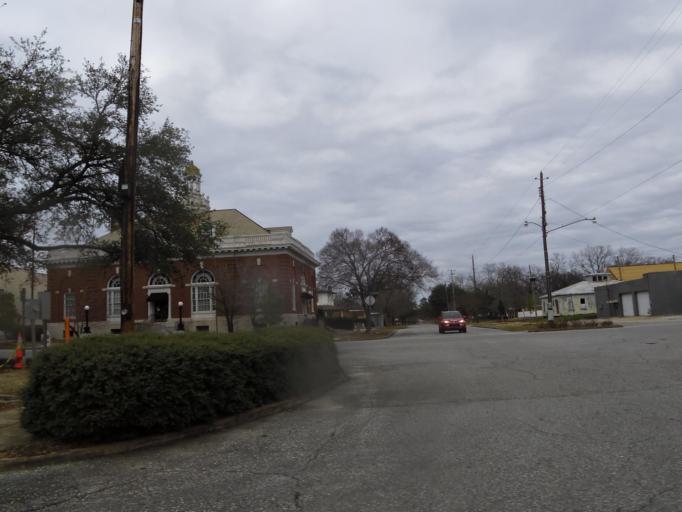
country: US
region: Alabama
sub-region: Barbour County
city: Eufaula
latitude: 31.8930
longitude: -85.1423
